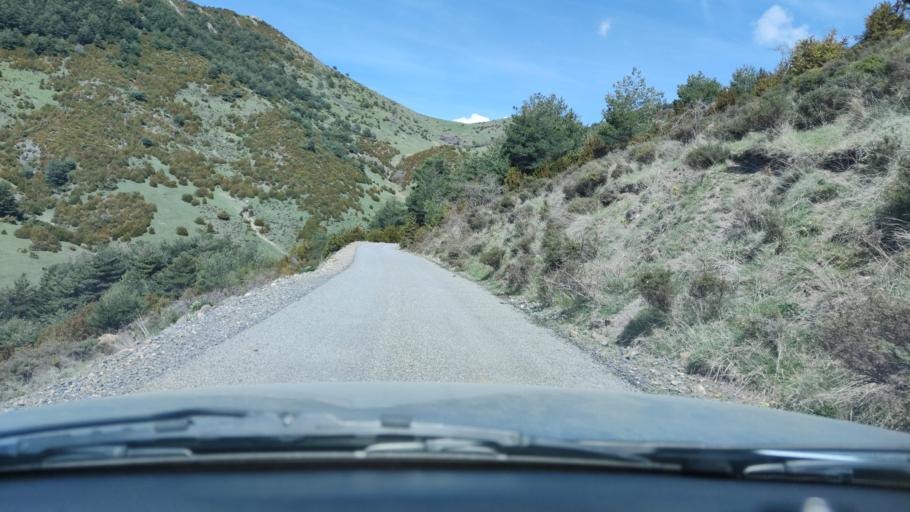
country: ES
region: Catalonia
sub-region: Provincia de Lleida
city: Sort
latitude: 42.3111
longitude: 1.1651
